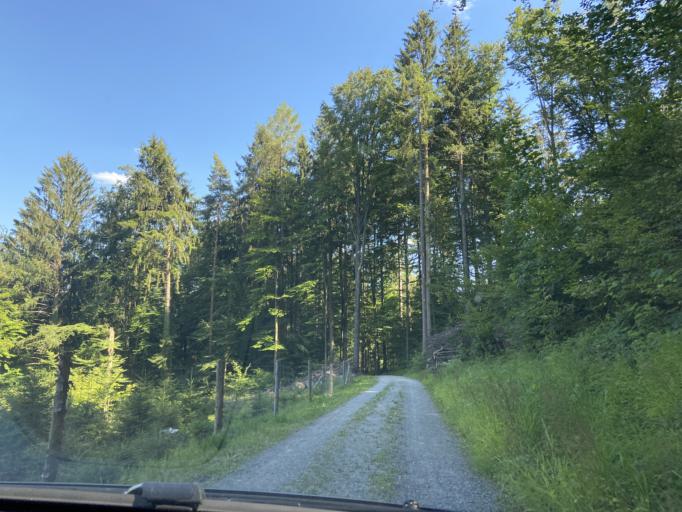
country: CH
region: Zurich
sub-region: Bezirk Winterthur
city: Wuelflingen (Kreis 6) / Niederfeld
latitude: 47.5042
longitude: 8.6673
